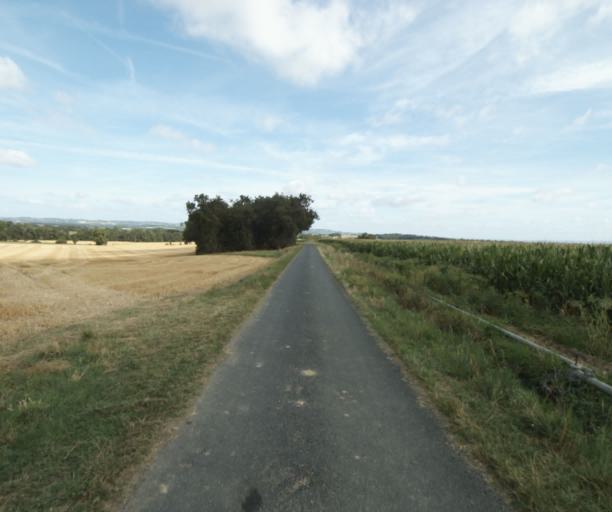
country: FR
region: Midi-Pyrenees
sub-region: Departement du Tarn
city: Soreze
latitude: 43.4828
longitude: 2.0888
